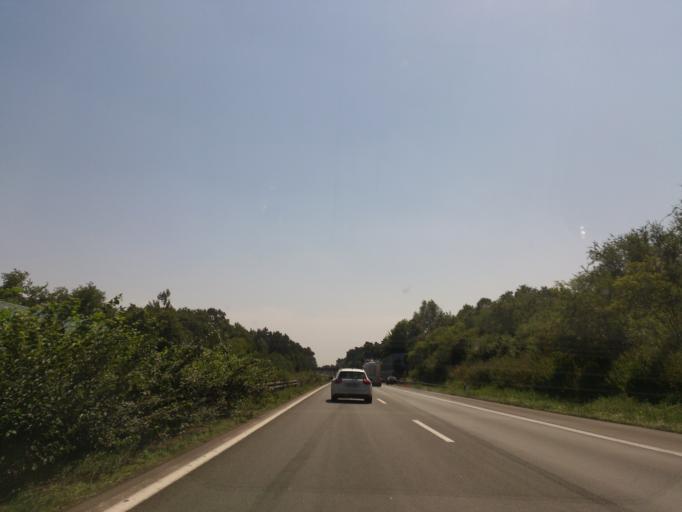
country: DE
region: North Rhine-Westphalia
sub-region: Regierungsbezirk Detmold
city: Oerlinghausen
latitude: 51.8915
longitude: 8.6405
